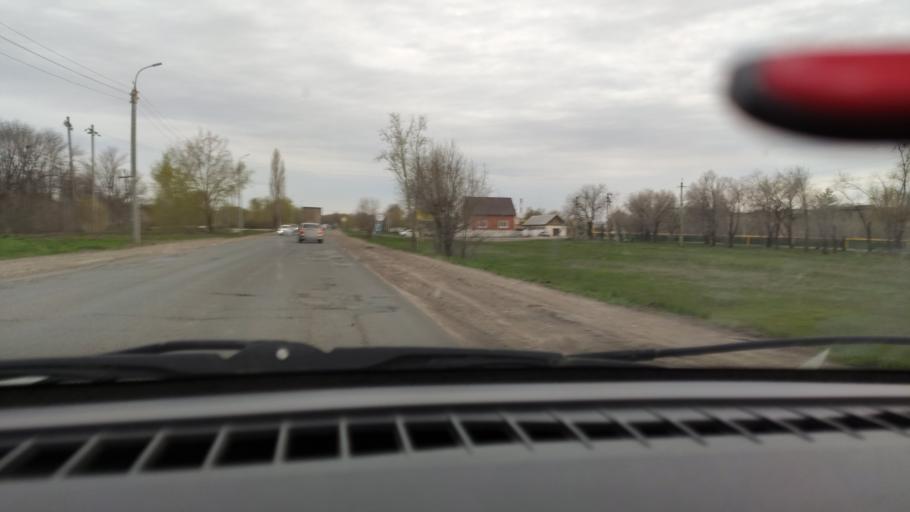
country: RU
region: Orenburg
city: Tatarskaya Kargala
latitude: 51.8644
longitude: 55.1385
